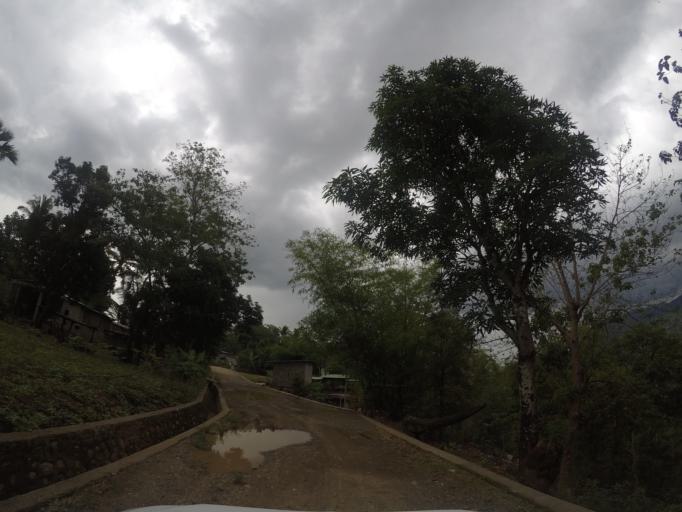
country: TL
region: Bobonaro
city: Maliana
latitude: -8.9750
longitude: 125.2206
